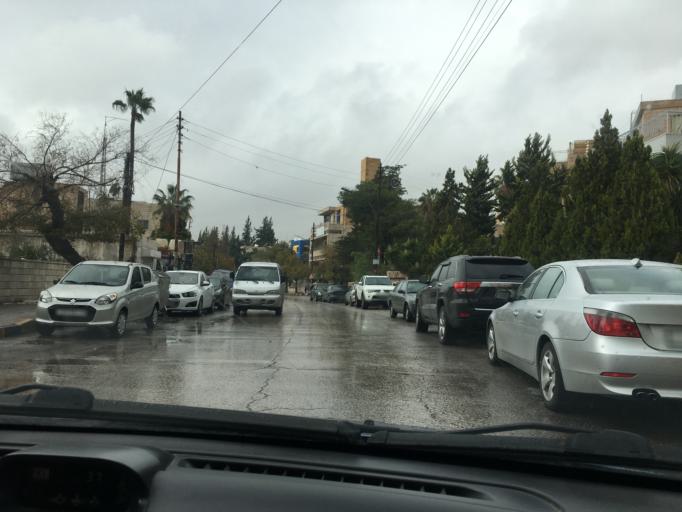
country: JO
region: Amman
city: Amman
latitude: 31.9640
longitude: 35.9163
